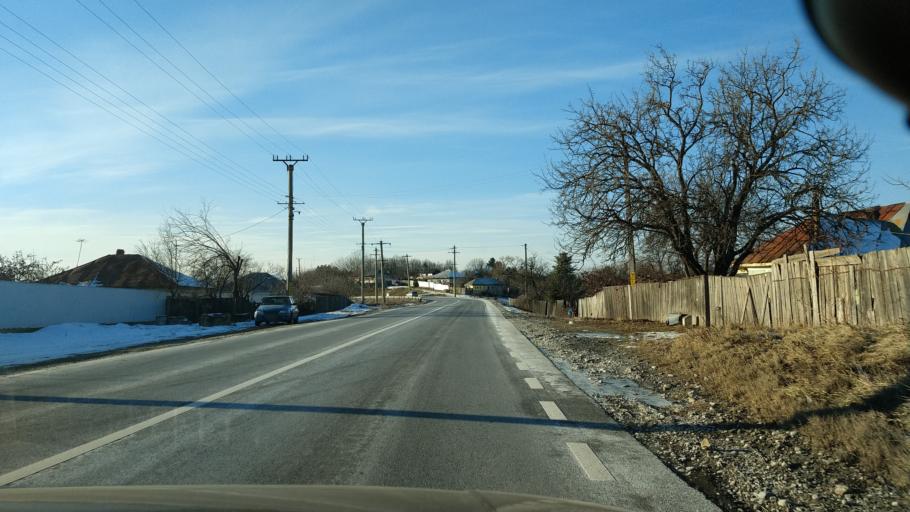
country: RO
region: Bacau
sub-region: Comuna Luizi-Calugara
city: Luizi-Calugara
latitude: 46.4922
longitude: 26.7840
